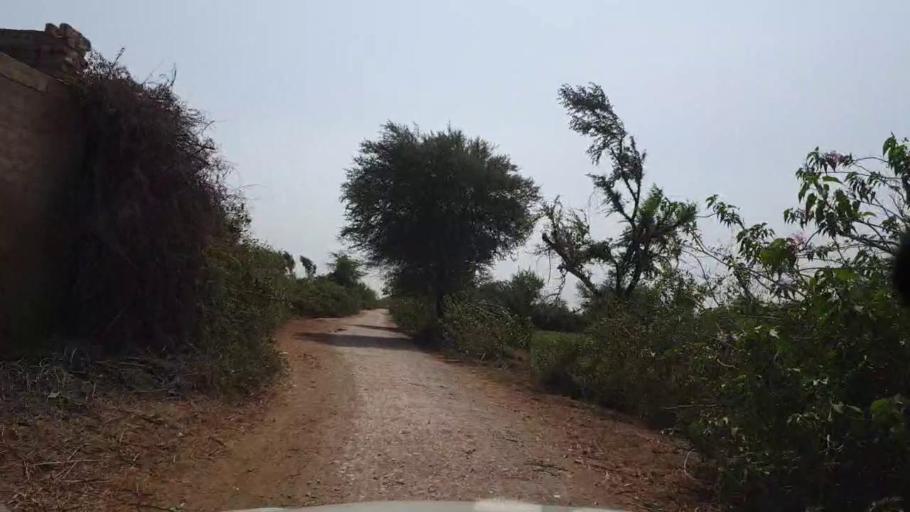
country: PK
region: Sindh
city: Matli
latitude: 25.0346
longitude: 68.7036
